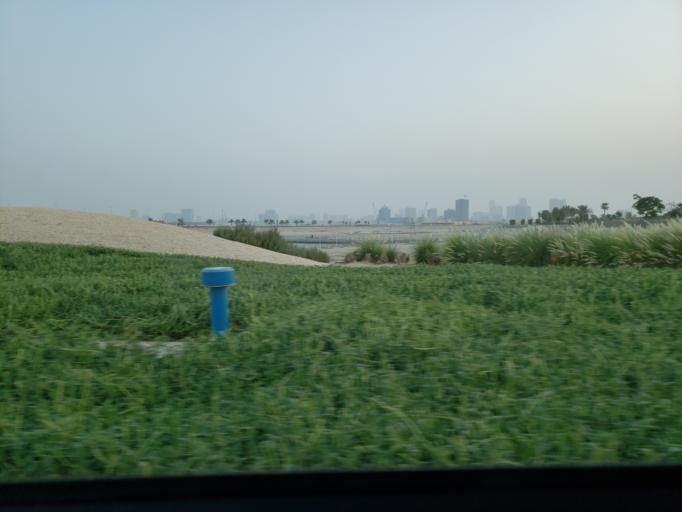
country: AE
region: Ajman
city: Ajman
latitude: 25.4342
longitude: 55.4647
